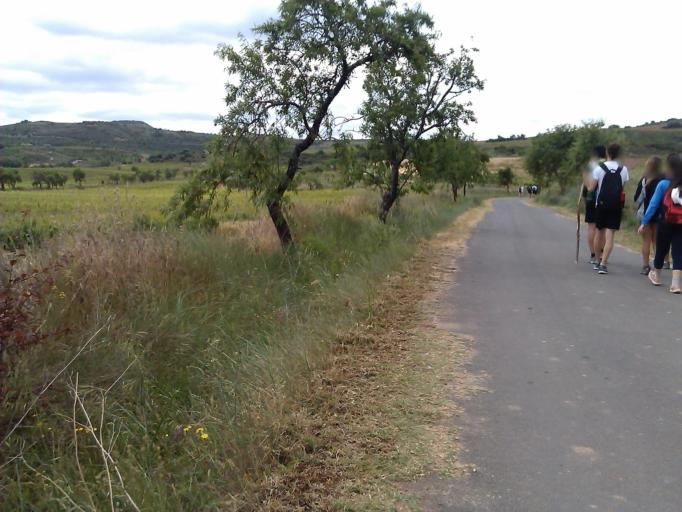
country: ES
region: La Rioja
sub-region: Provincia de La Rioja
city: Navarrete
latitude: 42.4406
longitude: -2.5149
